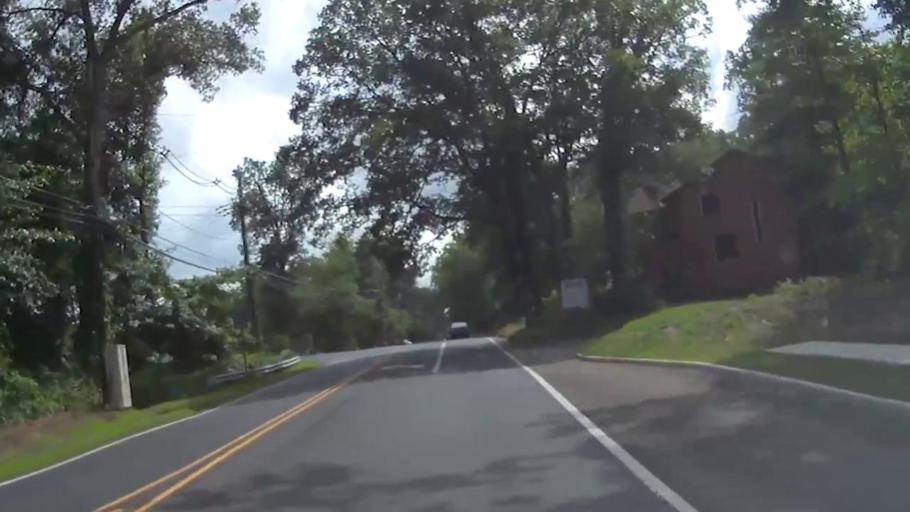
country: US
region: New Jersey
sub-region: Burlington County
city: Medford Lakes
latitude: 39.8673
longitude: -74.8480
